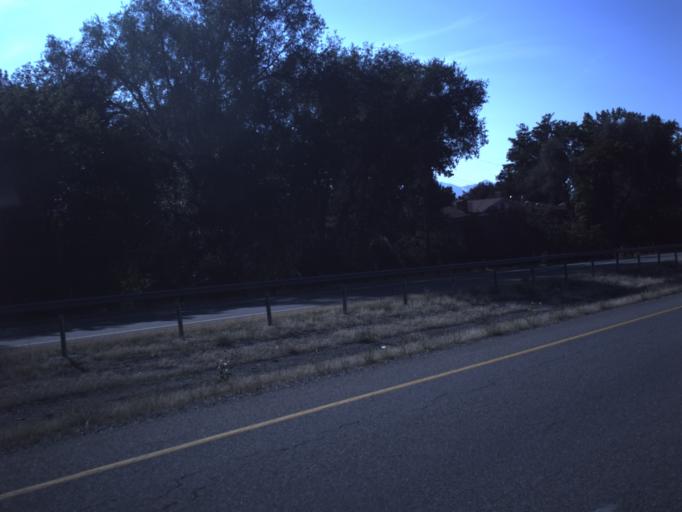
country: US
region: Utah
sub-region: Salt Lake County
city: Holladay
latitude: 40.6442
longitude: -111.8425
